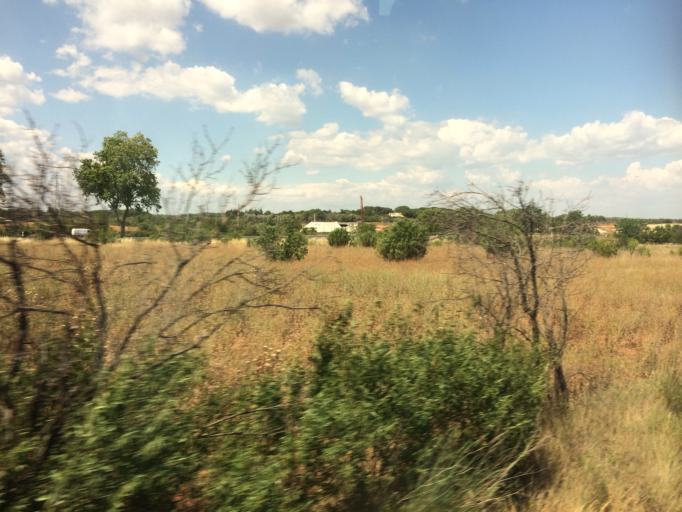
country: FR
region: Languedoc-Roussillon
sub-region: Departement de l'Herault
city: Valergues
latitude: 43.6696
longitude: 4.0519
